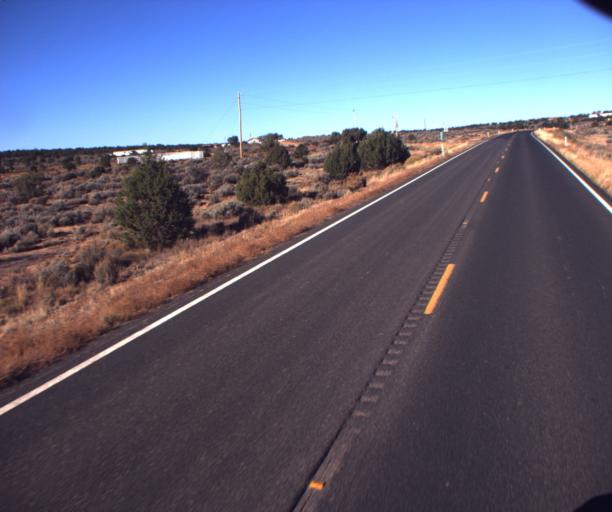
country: US
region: Arizona
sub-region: Apache County
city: Ganado
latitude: 35.7612
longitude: -109.7794
